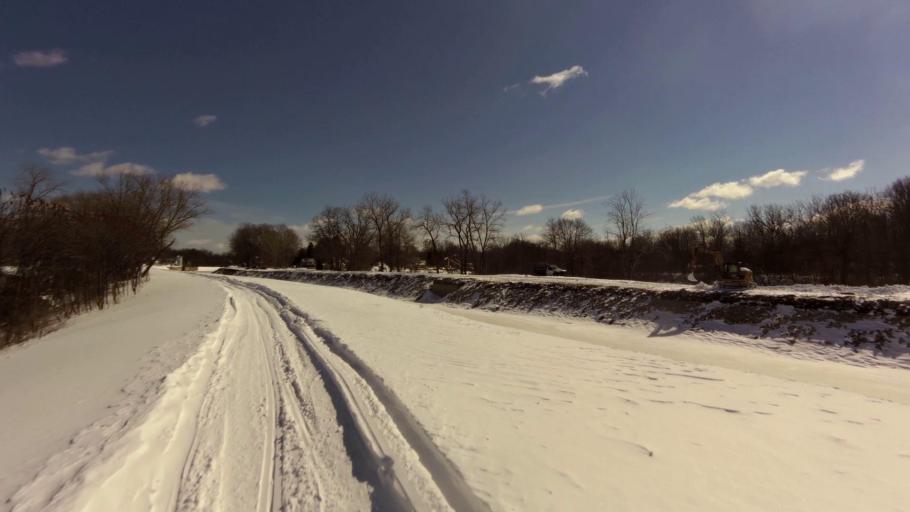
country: US
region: New York
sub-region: Orleans County
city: Holley
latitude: 43.2530
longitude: -78.0708
